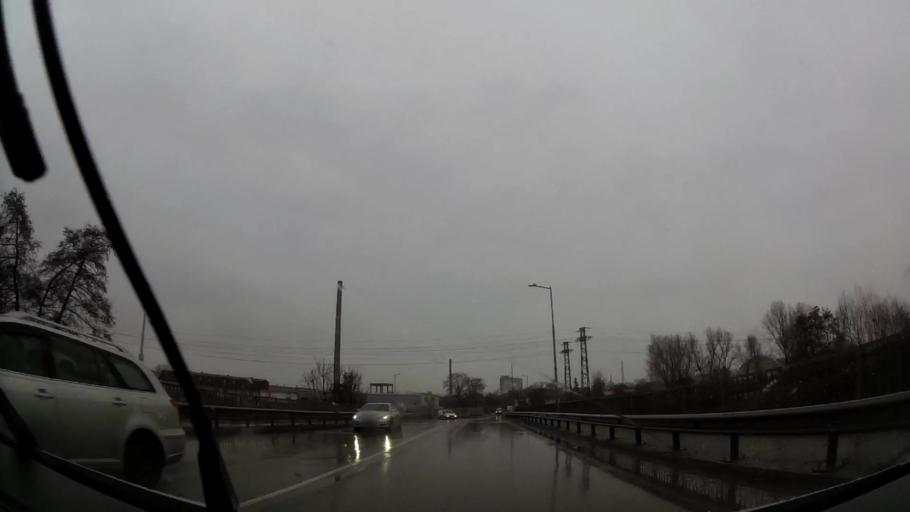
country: BG
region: Sofia-Capital
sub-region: Stolichna Obshtina
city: Sofia
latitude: 42.6651
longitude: 23.4206
